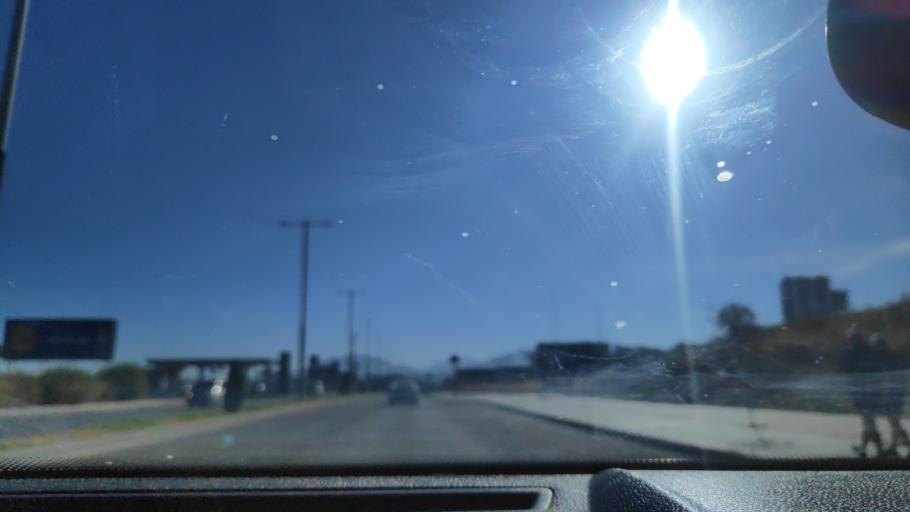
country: ES
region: Andalusia
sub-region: Provincia de Jaen
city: Jaen
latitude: 37.7917
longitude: -3.7856
